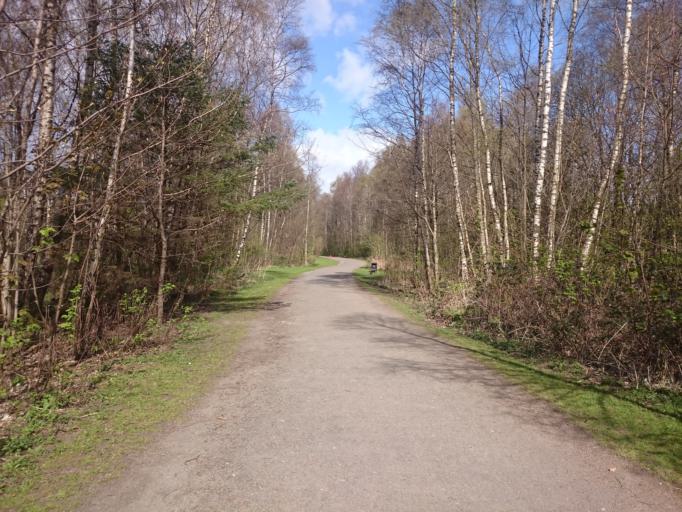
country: GB
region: Scotland
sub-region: West Dunbartonshire
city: Balloch
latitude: 56.0041
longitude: -4.5837
